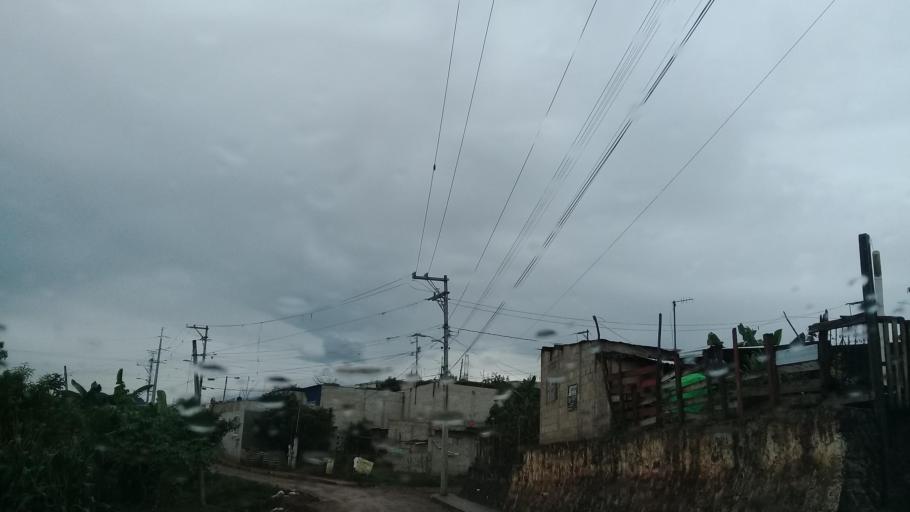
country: MX
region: Veracruz
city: El Castillo
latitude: 19.5670
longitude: -96.8879
